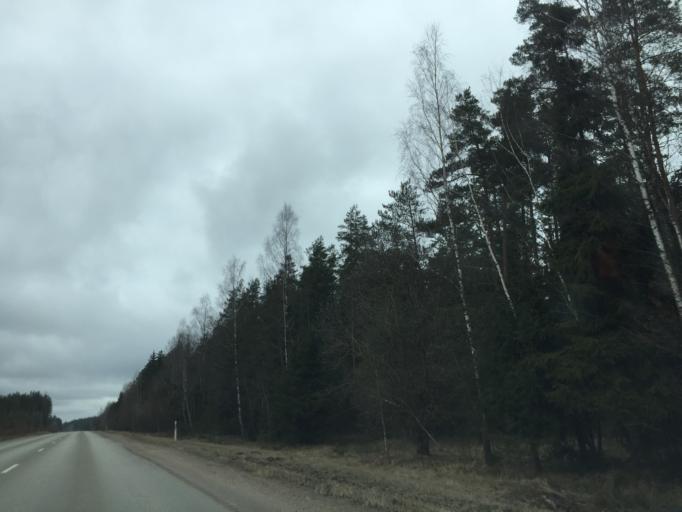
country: LV
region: Ilukste
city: Ilukste
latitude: 55.9106
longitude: 26.3592
